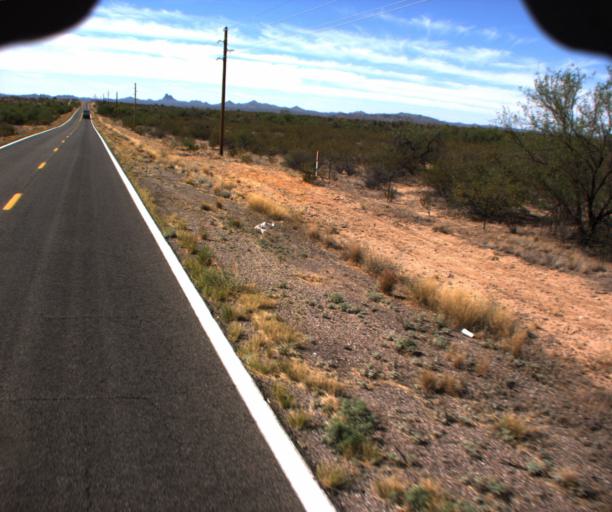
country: US
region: Arizona
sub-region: Yavapai County
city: Congress
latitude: 34.0719
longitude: -112.8219
